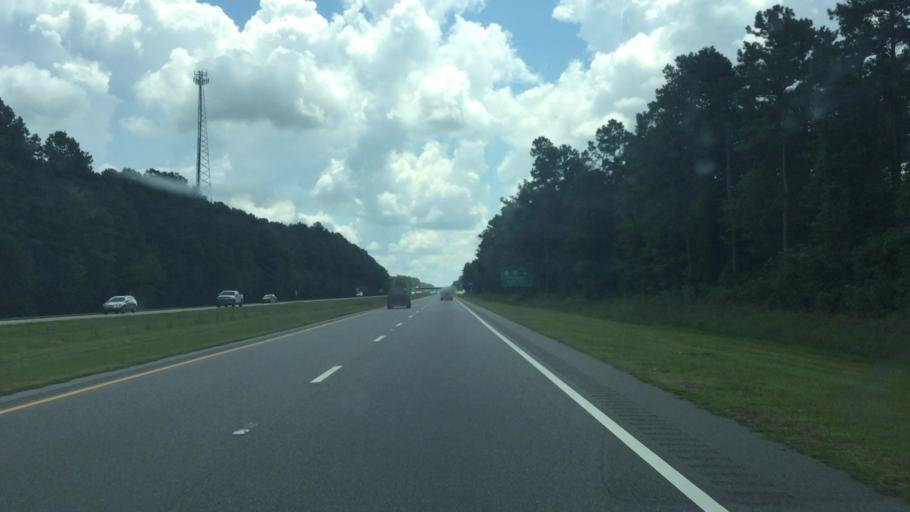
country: US
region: North Carolina
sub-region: Columbus County
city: Chadbourn
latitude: 34.3695
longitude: -78.8403
